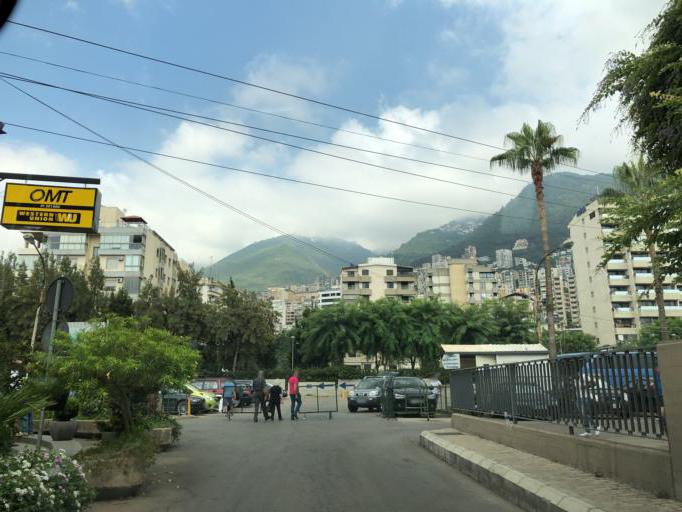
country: LB
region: Mont-Liban
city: Djounie
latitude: 33.9932
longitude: 35.6409
